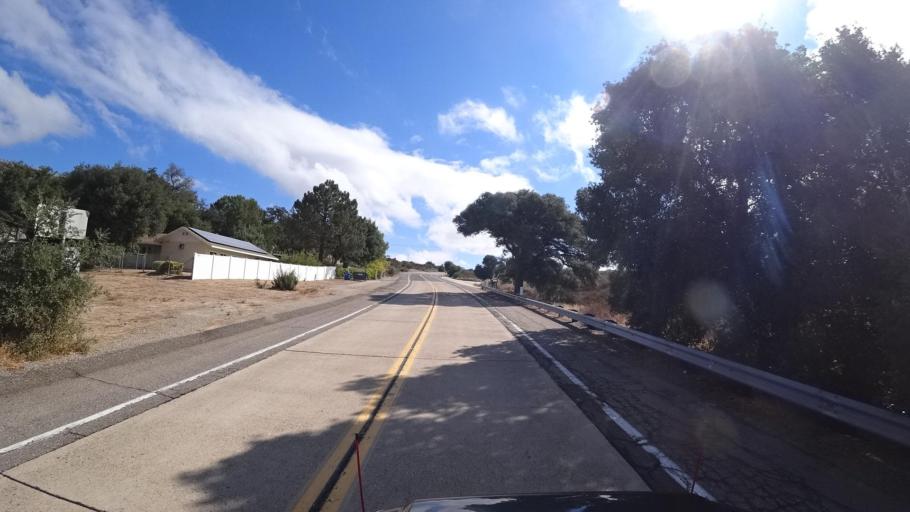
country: US
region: California
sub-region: San Diego County
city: Campo
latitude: 32.7042
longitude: -116.3640
